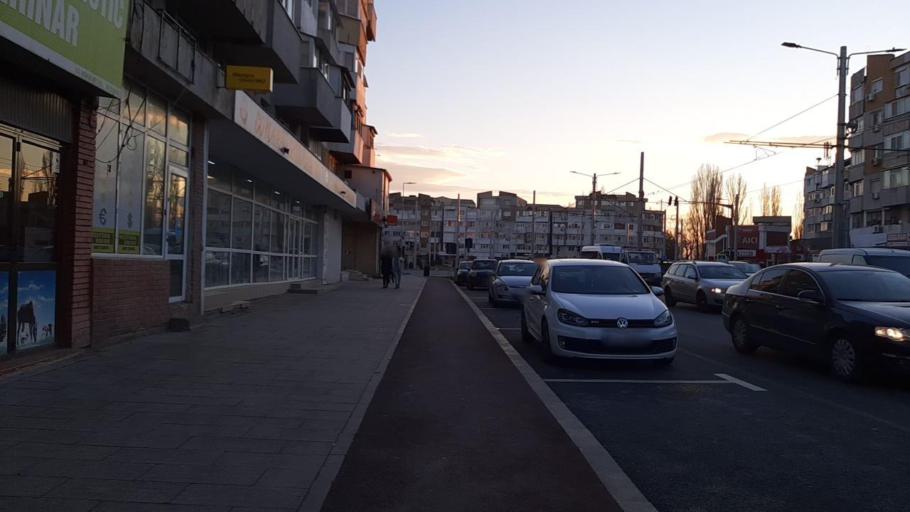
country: RO
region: Galati
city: Galati
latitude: 45.4413
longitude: 28.0212
